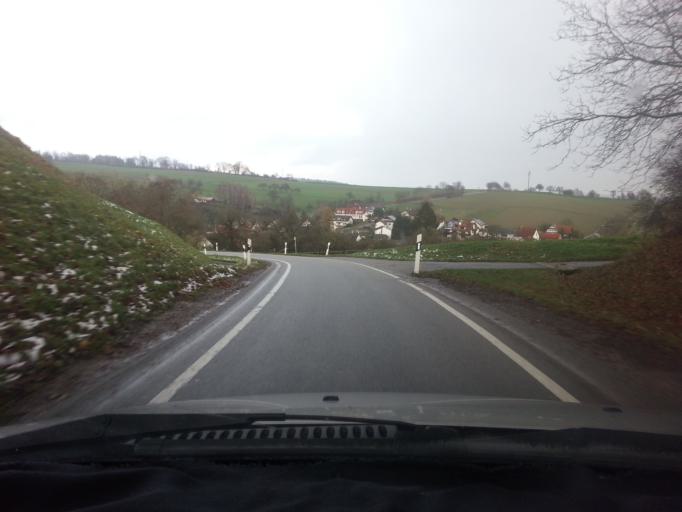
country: DE
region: Baden-Wuerttemberg
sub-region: Karlsruhe Region
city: Gaiberg
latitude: 49.3360
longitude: 8.7359
